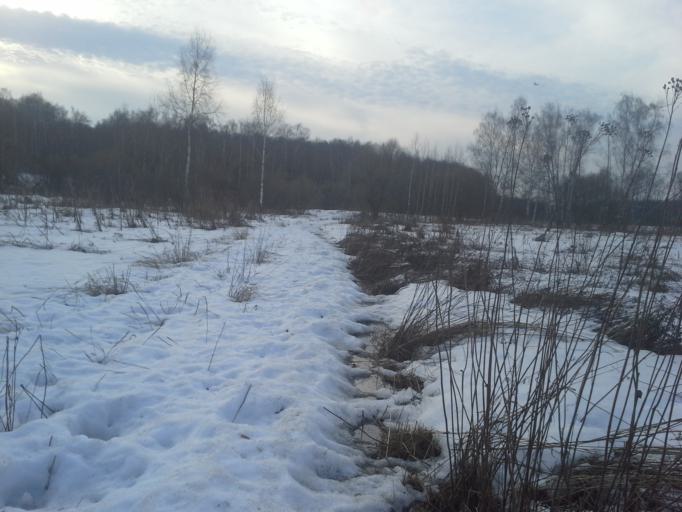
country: RU
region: Moscow
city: Yasenevo
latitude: 55.5939
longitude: 37.5086
